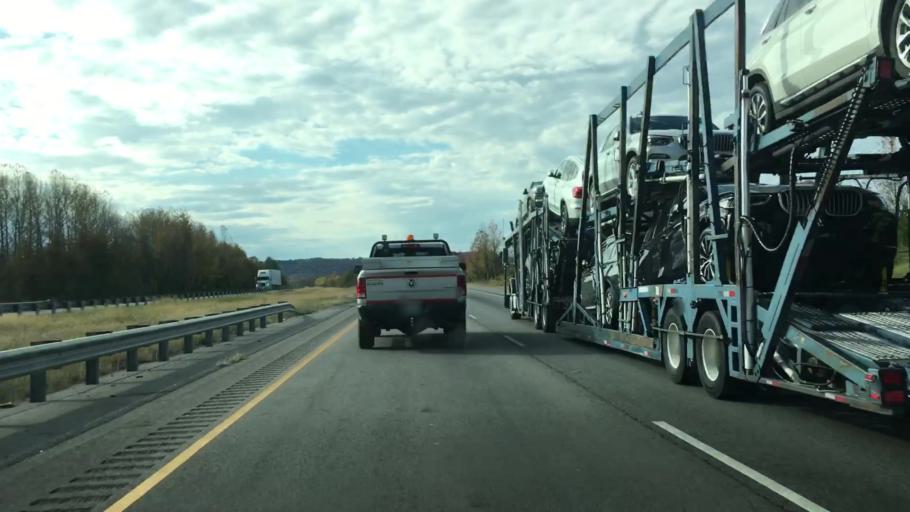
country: US
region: Arkansas
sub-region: Pope County
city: Atkins
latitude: 35.2510
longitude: -92.8899
